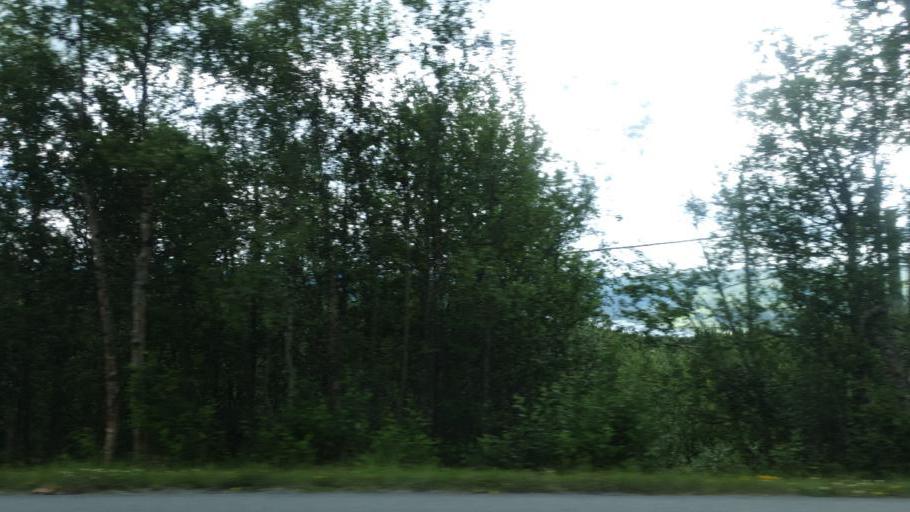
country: NO
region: Oppland
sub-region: Vestre Slidre
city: Slidre
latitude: 61.2501
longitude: 8.8961
